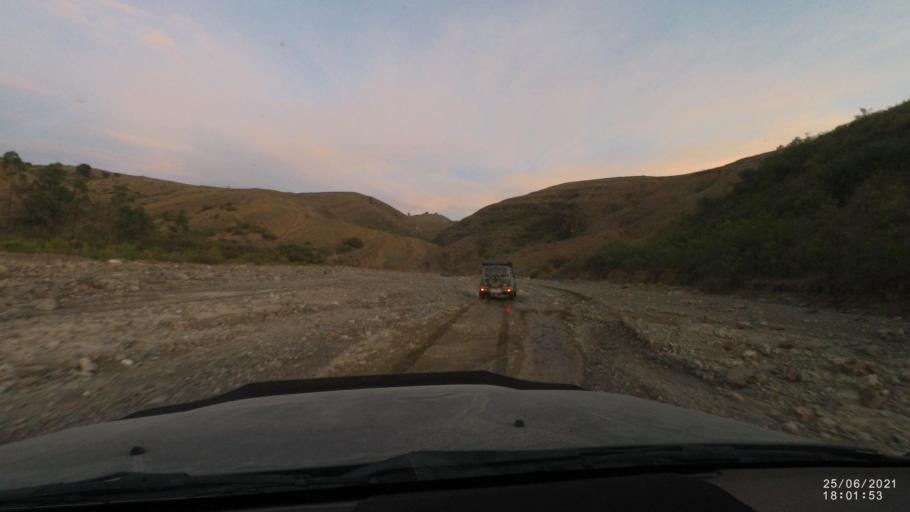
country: BO
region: Cochabamba
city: Mizque
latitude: -17.9471
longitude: -65.6347
